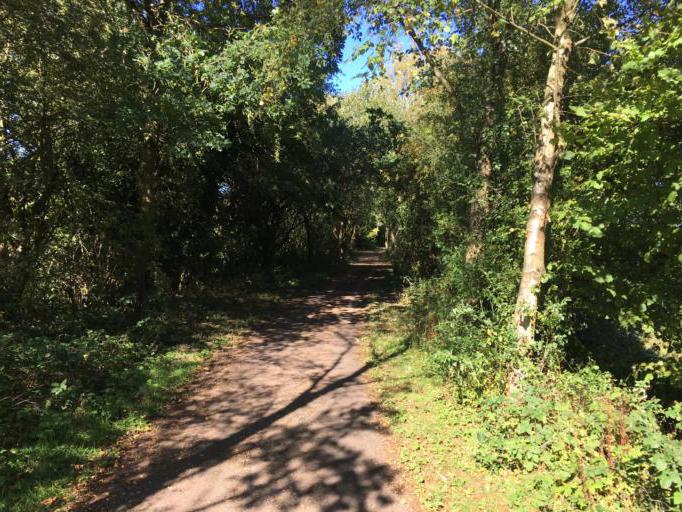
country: GB
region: England
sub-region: Warwickshire
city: Kenilworth
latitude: 52.3747
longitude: -1.5983
